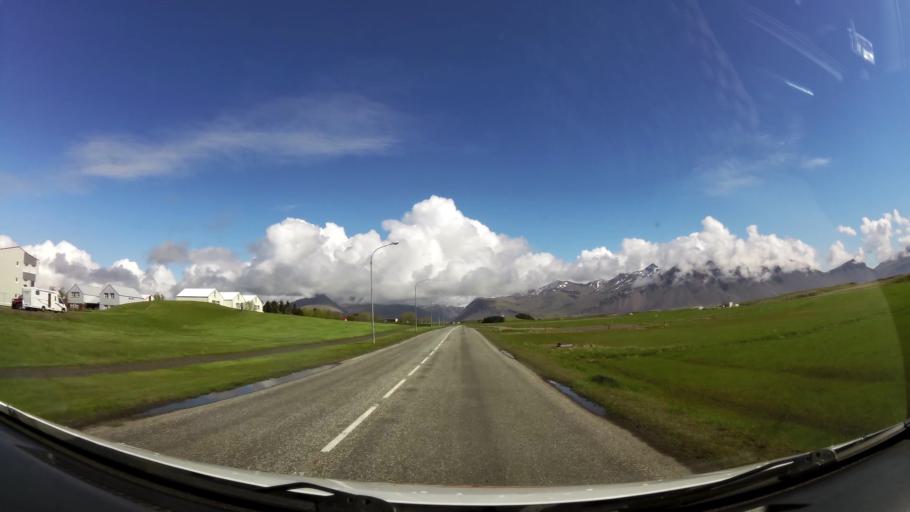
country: IS
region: East
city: Hoefn
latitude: 64.2598
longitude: -15.2043
